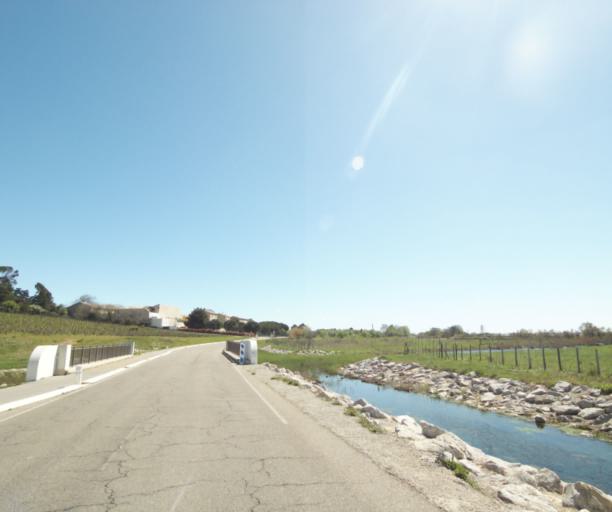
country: FR
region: Languedoc-Roussillon
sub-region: Departement de l'Herault
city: Lattes
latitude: 43.5640
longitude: 3.9197
